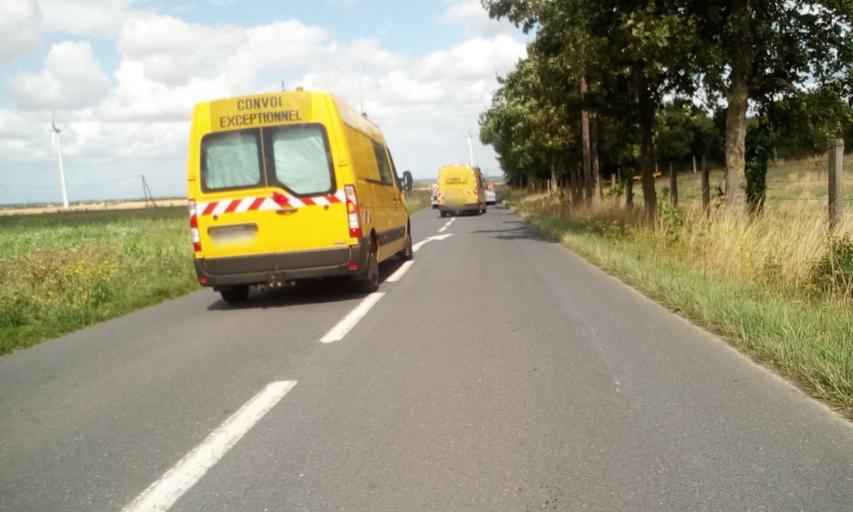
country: FR
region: Lower Normandy
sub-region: Departement du Calvados
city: Cagny
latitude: 49.1146
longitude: -0.2607
